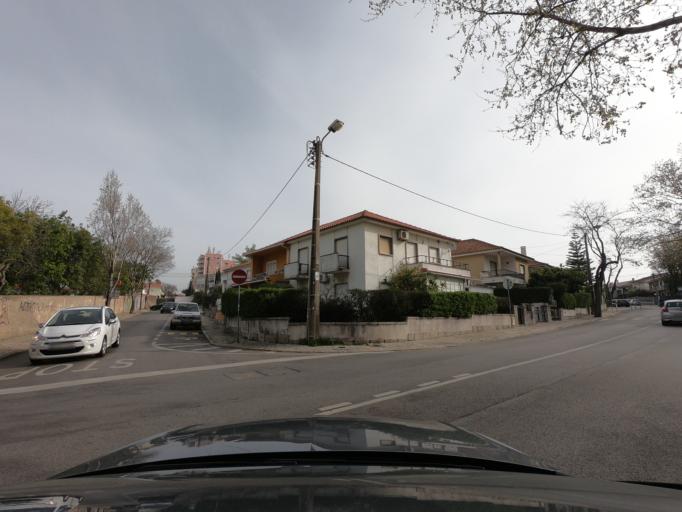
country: PT
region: Lisbon
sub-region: Cascais
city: Sao Domingos de Rana
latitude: 38.6978
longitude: -9.3278
